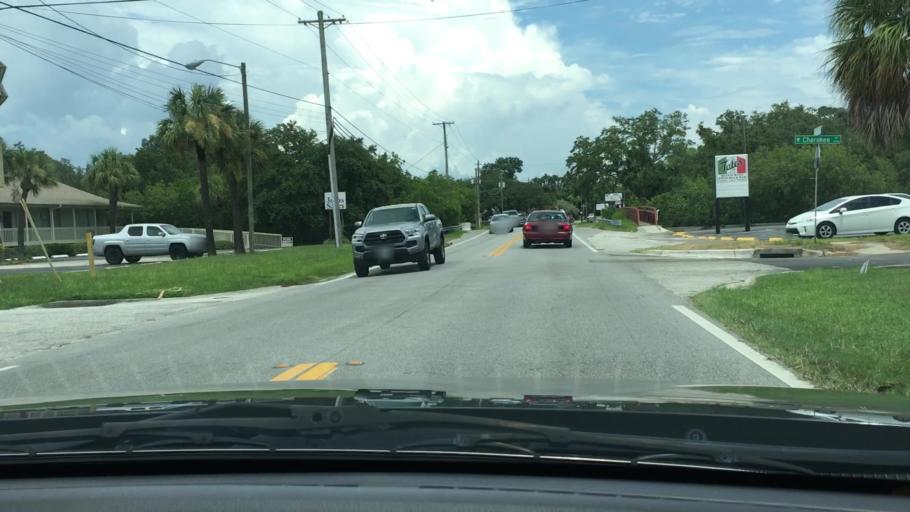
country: US
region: Florida
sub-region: Hillsborough County
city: Tampa
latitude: 27.9132
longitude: -82.5267
